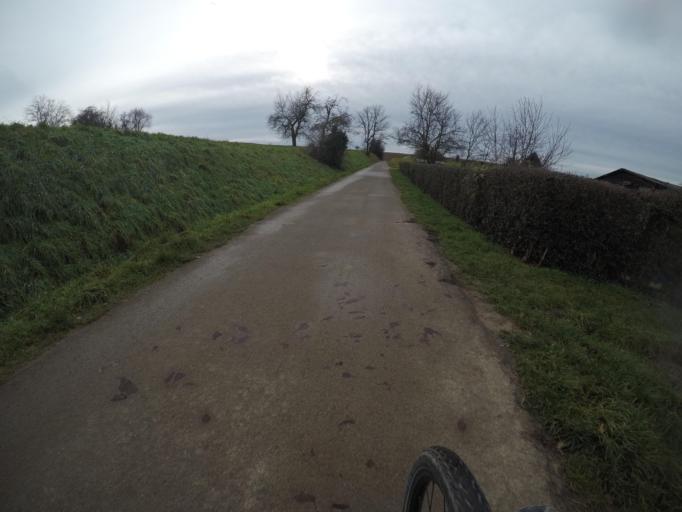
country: DE
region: Baden-Wuerttemberg
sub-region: Regierungsbezirk Stuttgart
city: Schwaikheim
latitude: 48.8718
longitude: 9.3434
